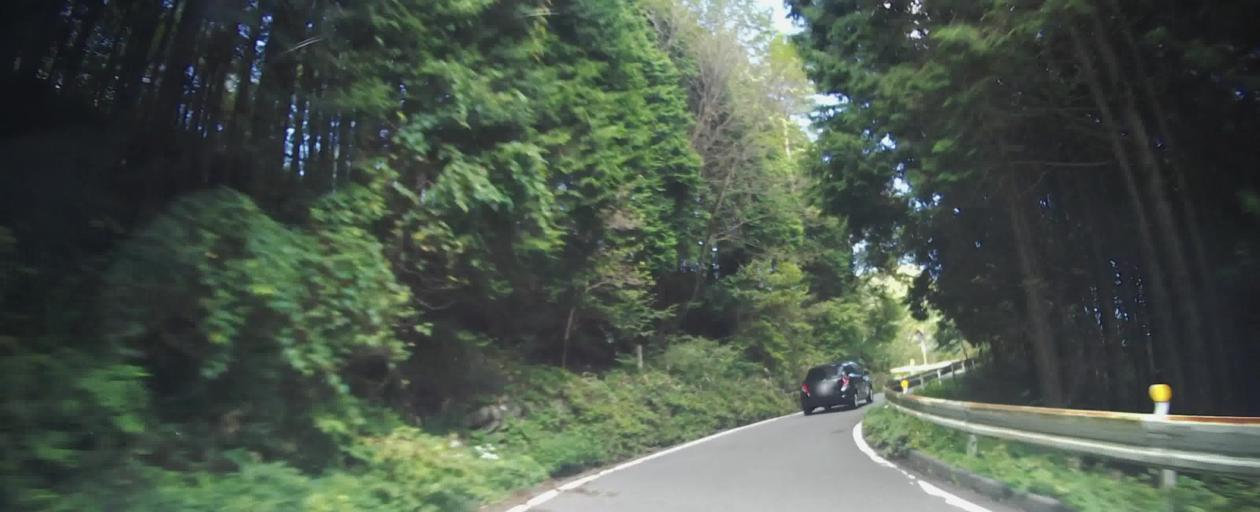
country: JP
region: Gunma
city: Shibukawa
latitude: 36.4658
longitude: 138.8890
